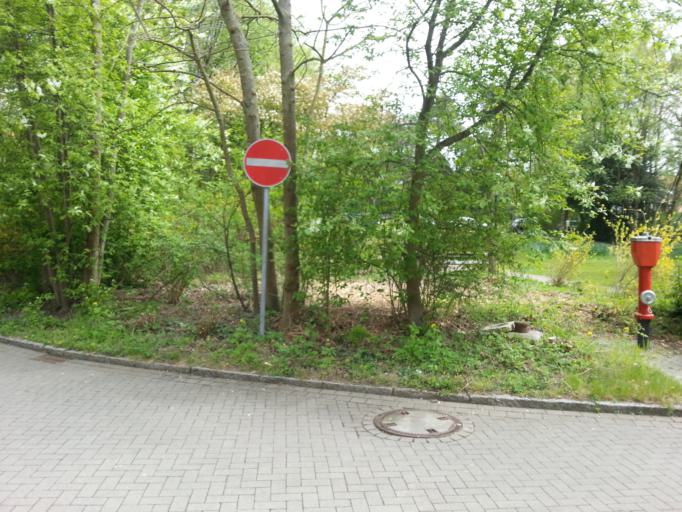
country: DE
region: Schleswig-Holstein
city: Luebeck
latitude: 53.8372
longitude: 10.7060
